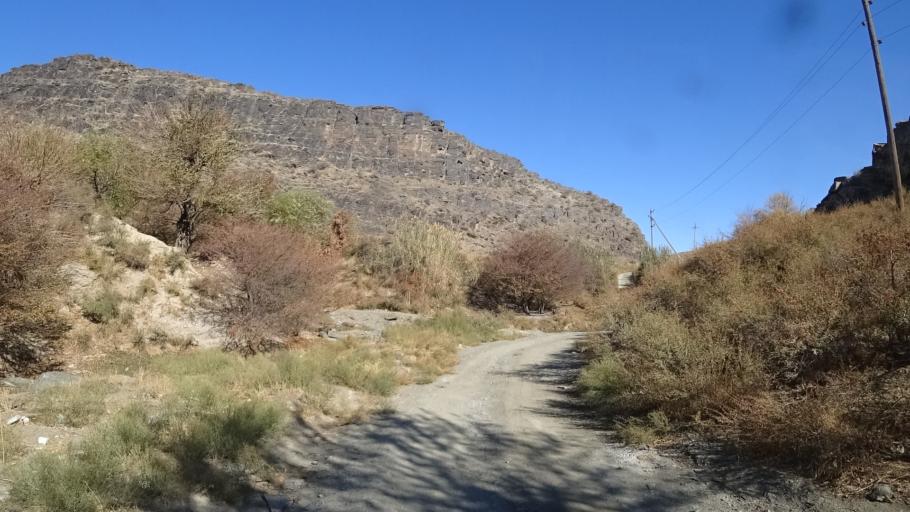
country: UZ
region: Navoiy
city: Nurota
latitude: 40.3095
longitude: 65.6211
